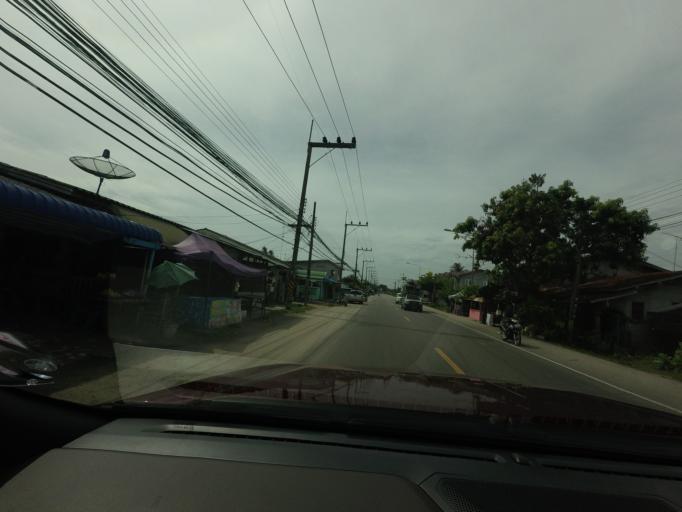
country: TH
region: Narathiwat
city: Tak Bai
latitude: 6.2532
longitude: 102.0625
